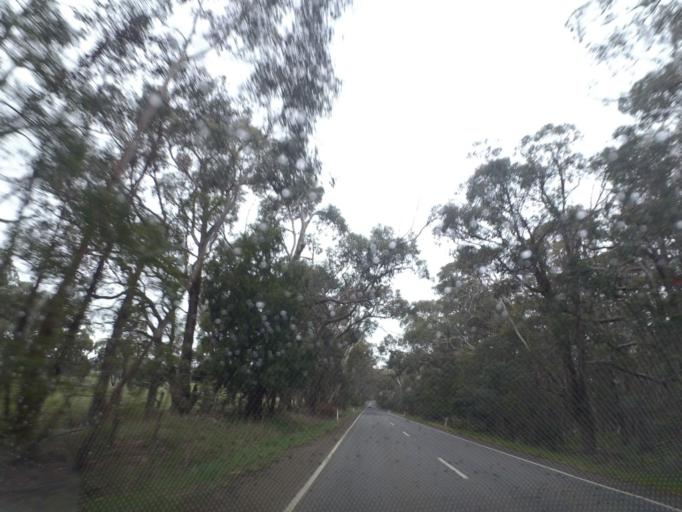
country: AU
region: Victoria
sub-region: Hume
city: Sunbury
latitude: -37.3447
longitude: 144.6863
